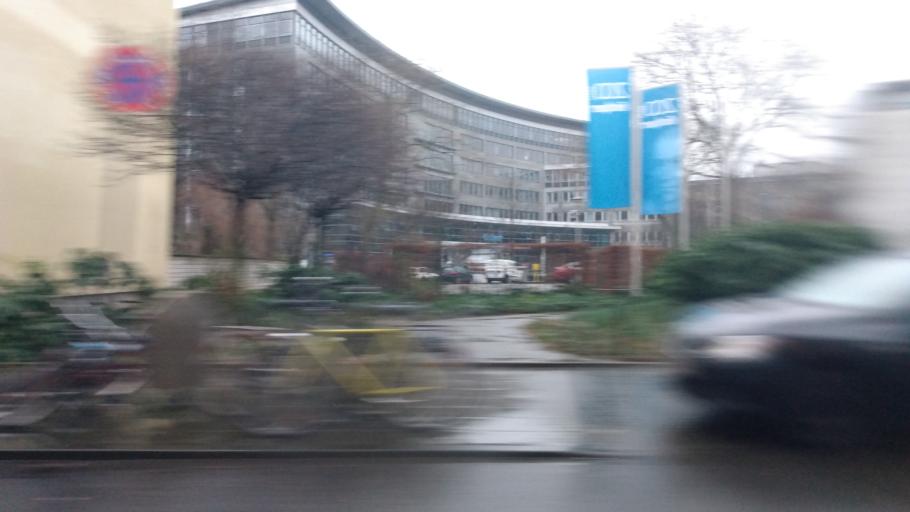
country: DE
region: North Rhine-Westphalia
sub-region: Regierungsbezirk Koln
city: Neustadt/Sued
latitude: 50.9153
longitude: 6.9411
